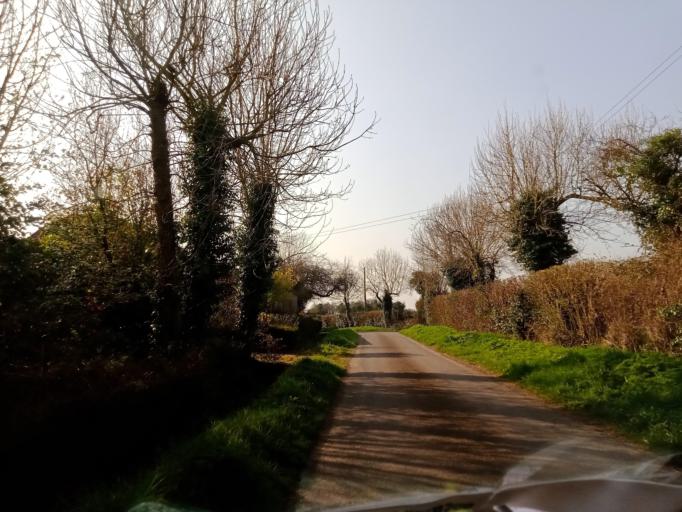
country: IE
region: Leinster
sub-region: Kilkenny
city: Callan
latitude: 52.5338
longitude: -7.3997
